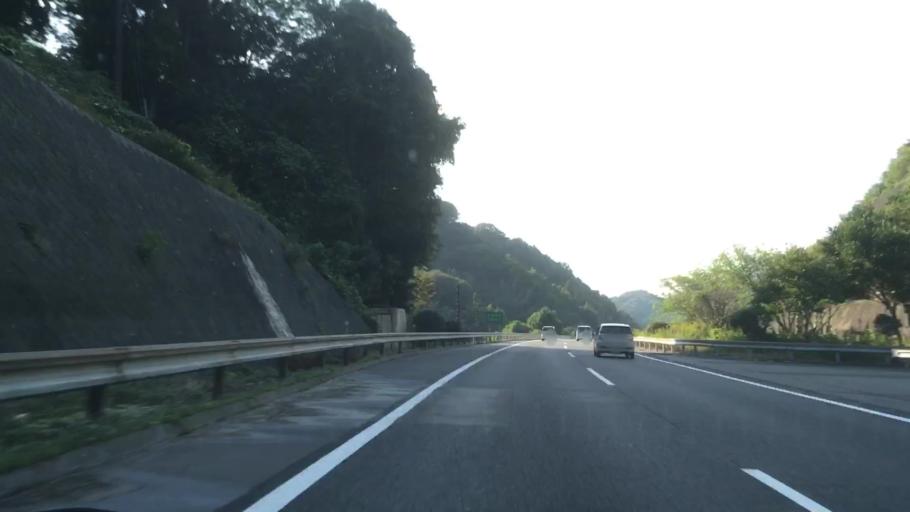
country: JP
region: Yamaguchi
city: Tokuyama
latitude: 34.0736
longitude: 131.8074
